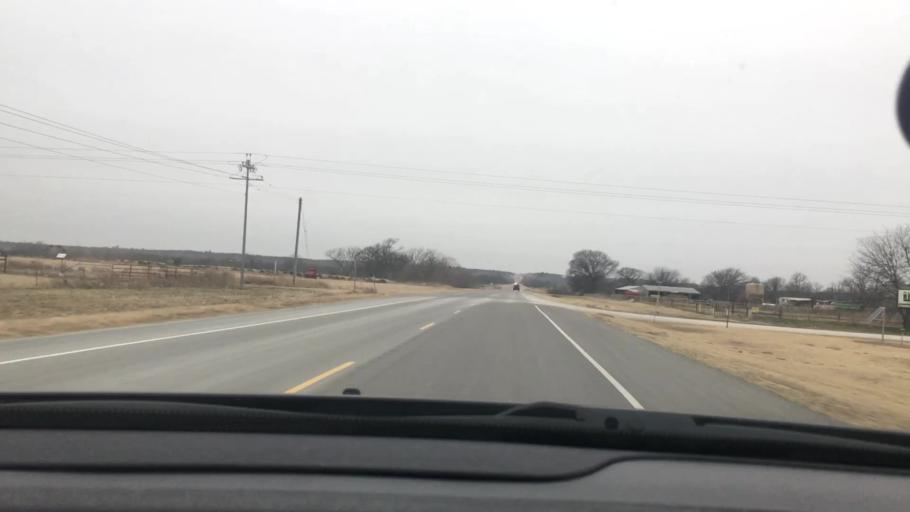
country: US
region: Oklahoma
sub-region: Garvin County
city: Wynnewood
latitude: 34.6226
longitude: -97.1767
